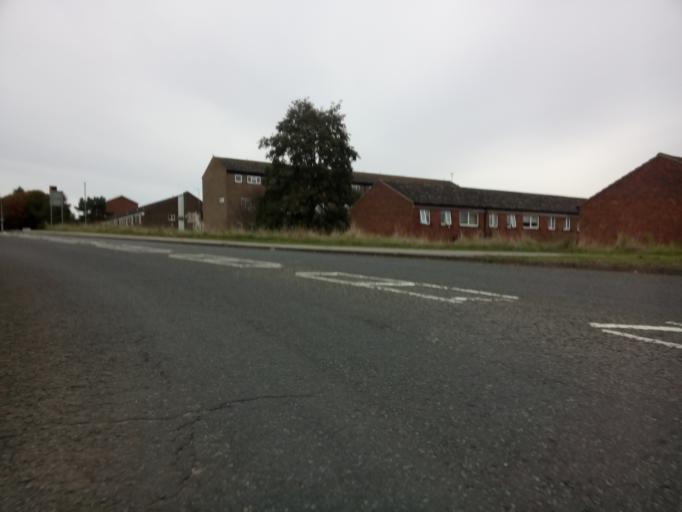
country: GB
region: England
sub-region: Suffolk
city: Ipswich
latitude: 52.0378
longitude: 1.1228
